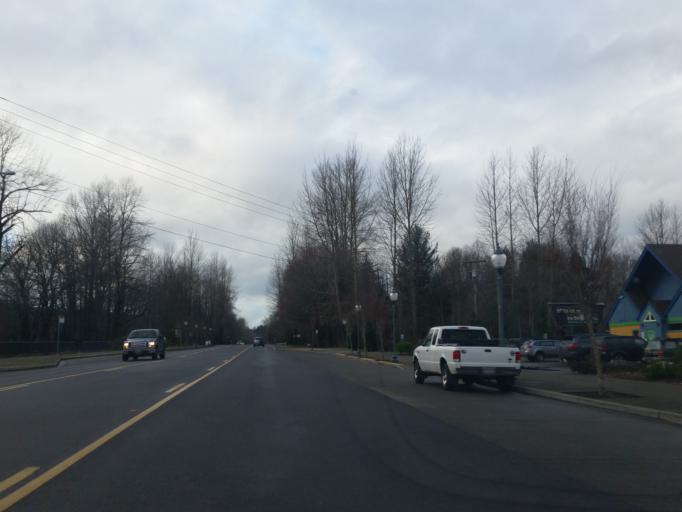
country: US
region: Washington
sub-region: King County
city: North Bend
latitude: 47.4962
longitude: -121.7882
